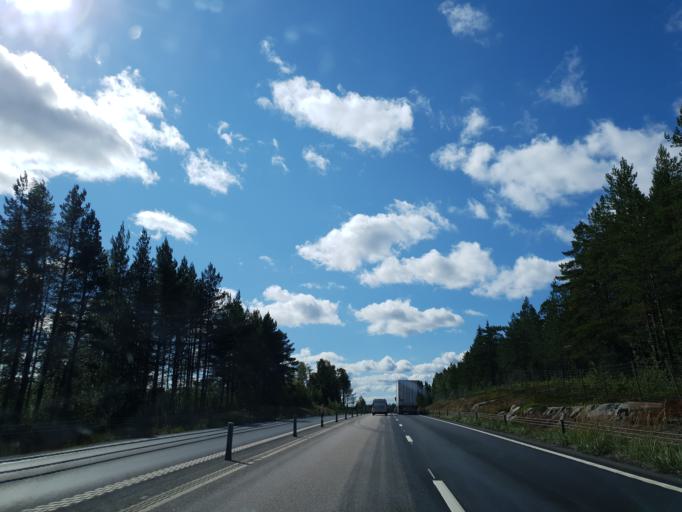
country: SE
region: Vaesterbotten
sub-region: Nordmalings Kommun
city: Nordmaling
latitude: 63.5204
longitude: 19.3763
